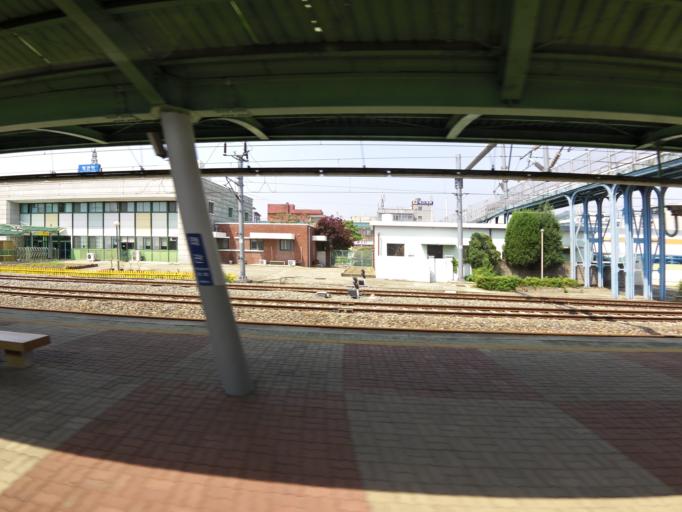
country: KR
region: Gyeongsangbuk-do
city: Waegwan
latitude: 35.9924
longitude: 128.4004
